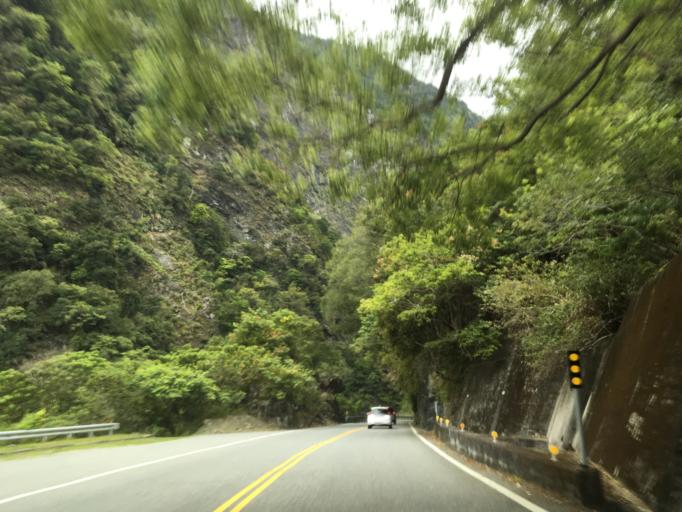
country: TW
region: Taiwan
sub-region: Hualien
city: Hualian
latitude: 24.1774
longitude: 121.5064
